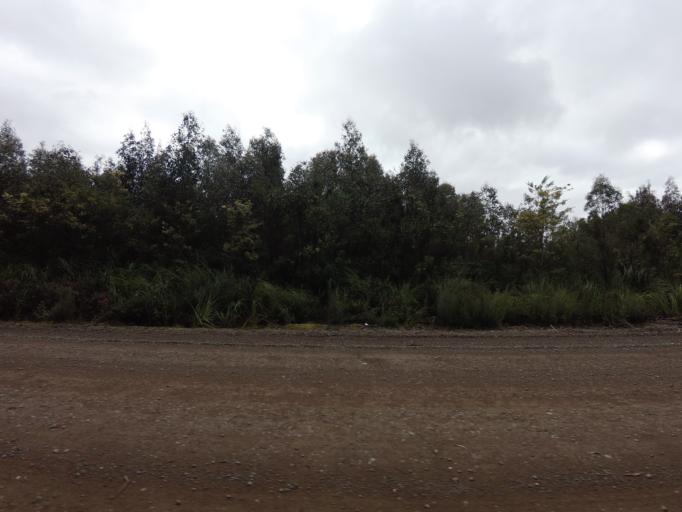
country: AU
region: Tasmania
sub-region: Huon Valley
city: Geeveston
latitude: -43.5099
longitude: 146.8845
